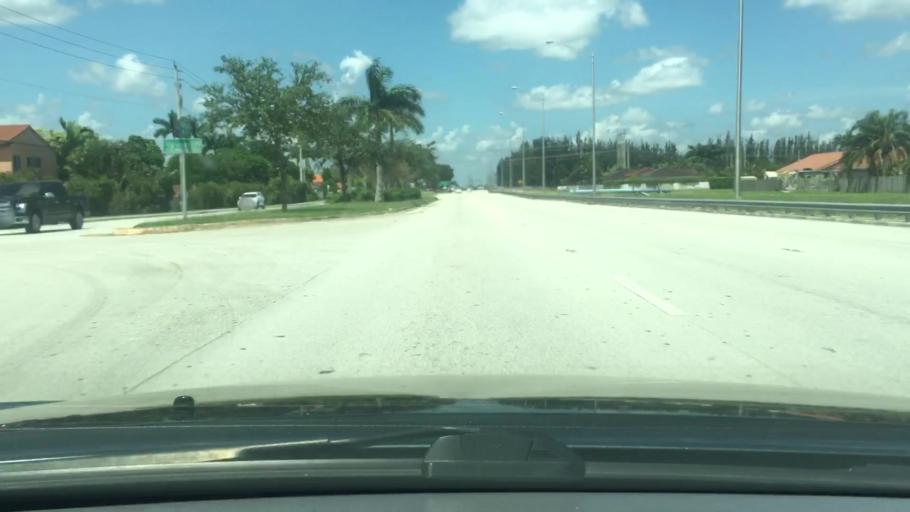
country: US
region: Florida
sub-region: Miami-Dade County
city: Tamiami
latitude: 25.7607
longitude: -80.4118
